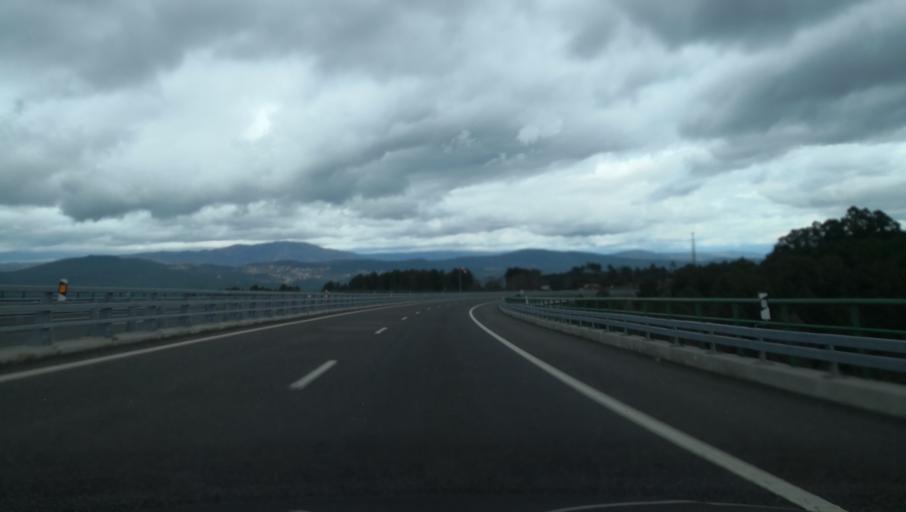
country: PT
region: Vila Real
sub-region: Boticas
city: Boticas
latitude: 41.6096
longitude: -7.6261
